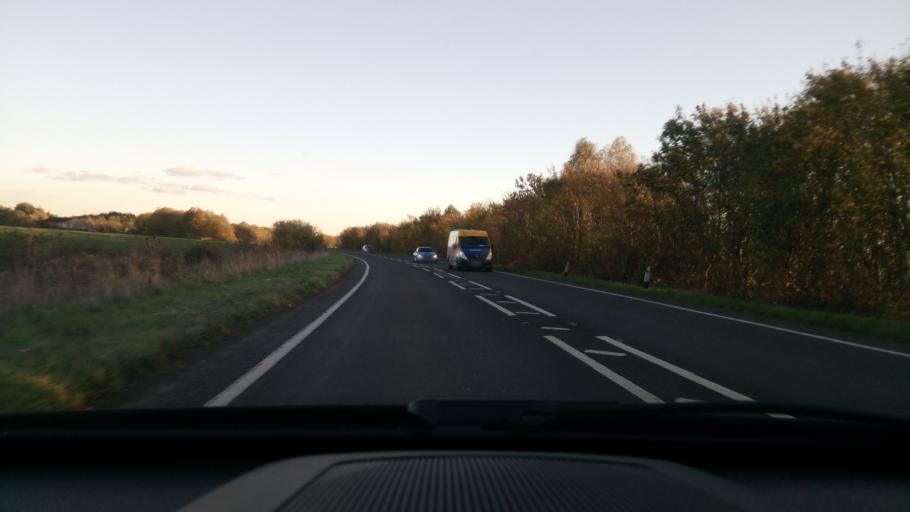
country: GB
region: England
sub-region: Peterborough
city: Glinton
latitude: 52.6348
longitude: -0.3061
